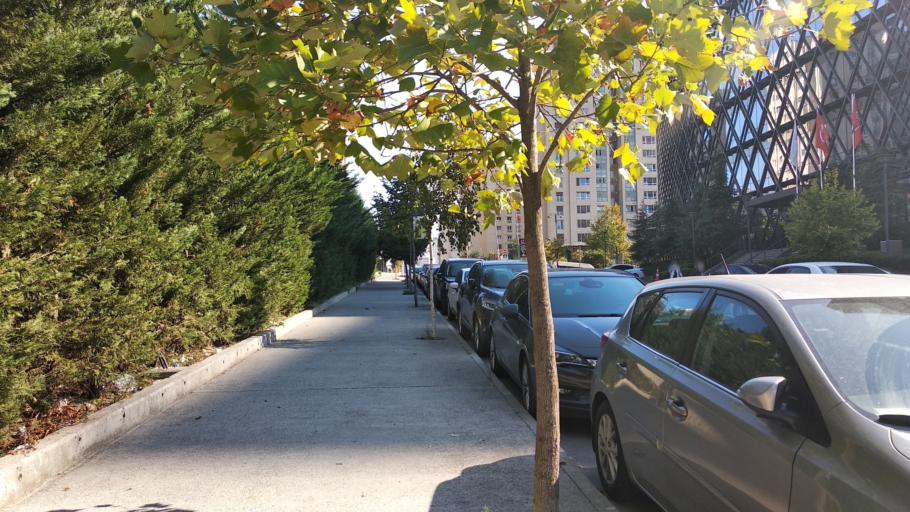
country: TR
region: Istanbul
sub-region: Atasehir
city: Atasehir
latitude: 40.9989
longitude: 29.1015
